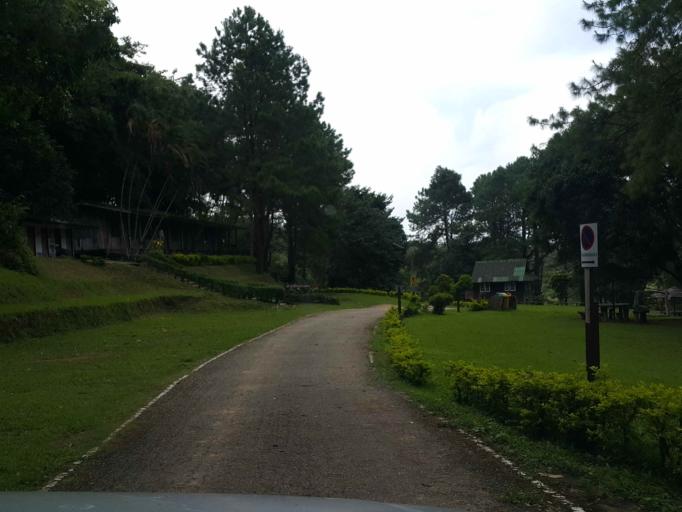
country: TH
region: Tak
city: Tak
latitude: 16.7816
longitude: 98.9281
